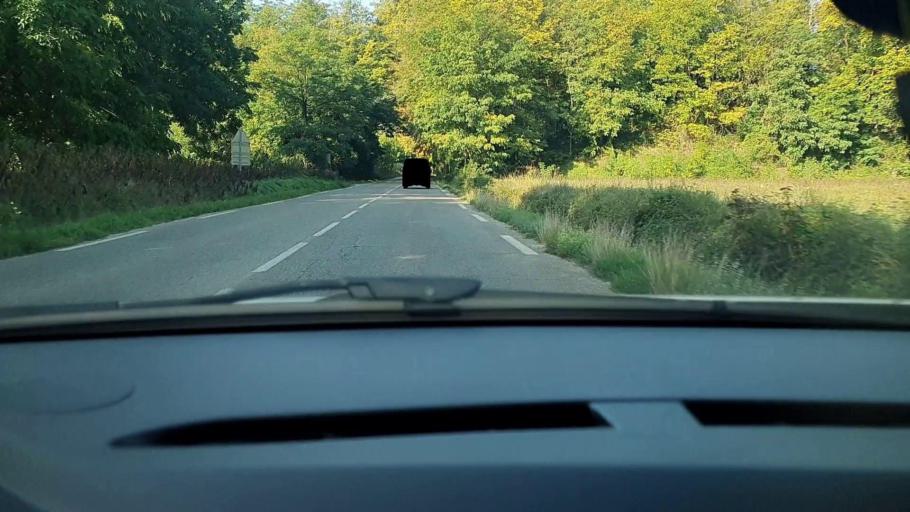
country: FR
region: Languedoc-Roussillon
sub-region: Departement du Gard
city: Besseges
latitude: 44.2841
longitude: 4.1217
